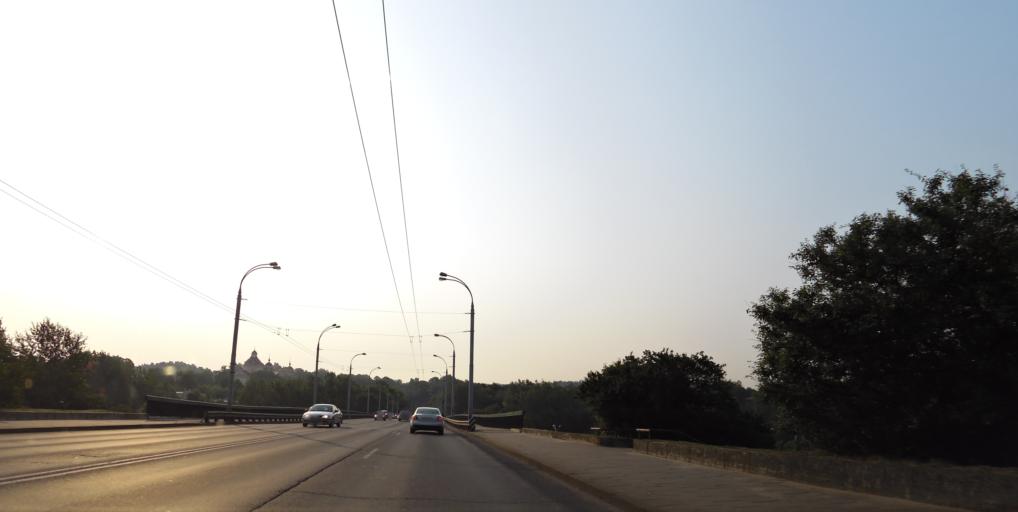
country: LT
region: Vilnius County
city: Rasos
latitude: 54.6953
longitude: 25.3002
